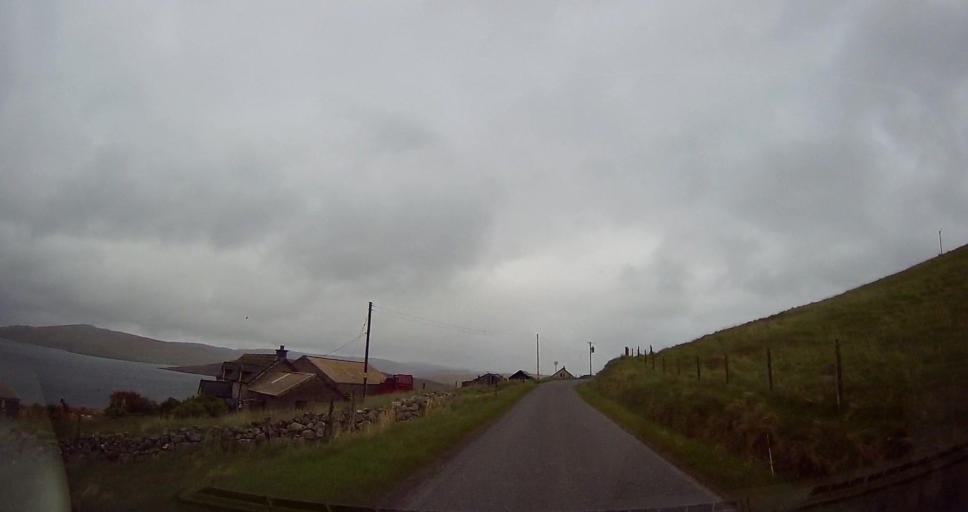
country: GB
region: Scotland
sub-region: Shetland Islands
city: Lerwick
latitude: 60.3711
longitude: -1.3828
